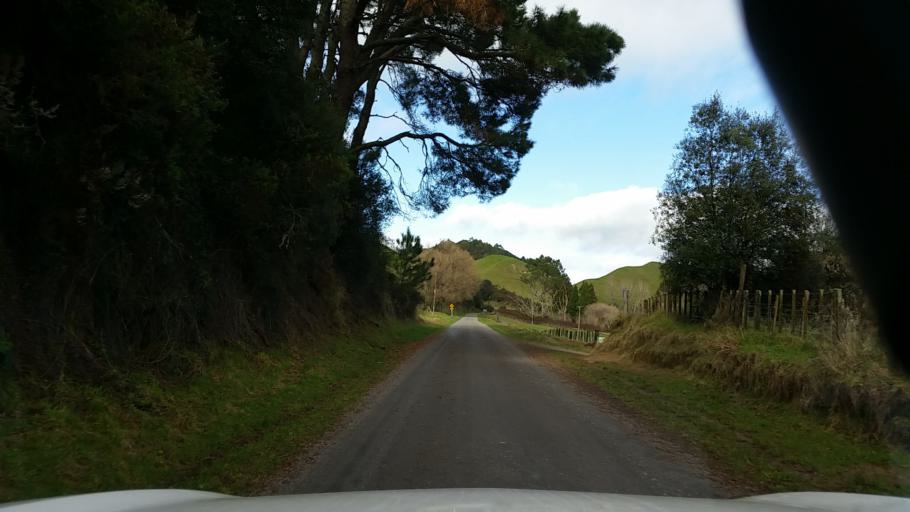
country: NZ
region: Waikato
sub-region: Taupo District
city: Taupo
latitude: -38.4618
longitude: 176.2411
